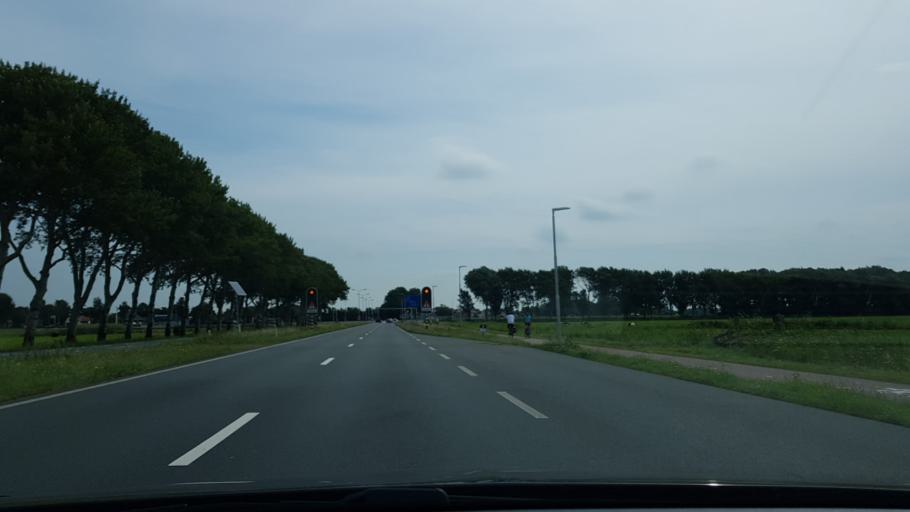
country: NL
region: North Holland
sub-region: Gemeente Castricum
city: Castricum
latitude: 52.5615
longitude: 4.6846
